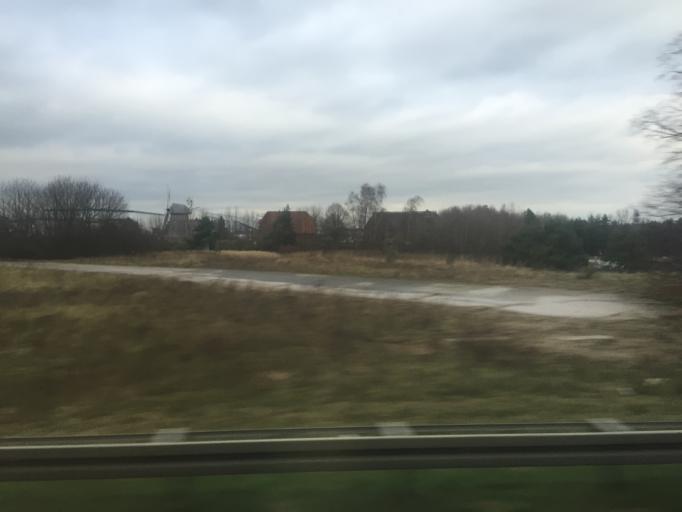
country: DE
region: Mecklenburg-Vorpommern
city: Wittenburg
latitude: 53.4980
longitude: 11.0937
